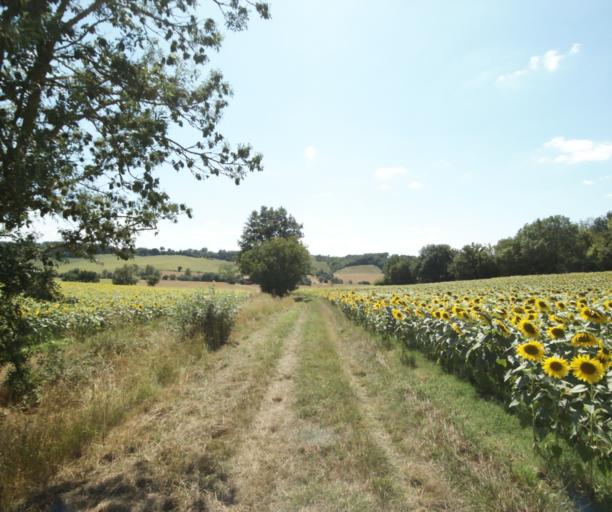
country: FR
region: Midi-Pyrenees
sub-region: Departement de la Haute-Garonne
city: Auriac-sur-Vendinelle
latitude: 43.5006
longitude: 1.8694
